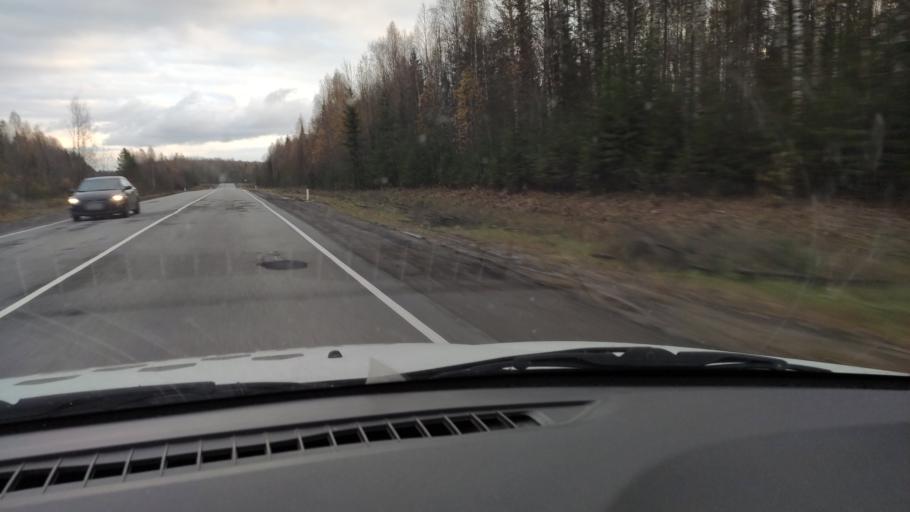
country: RU
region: Kirov
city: Omutninsk
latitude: 58.7532
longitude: 52.0485
